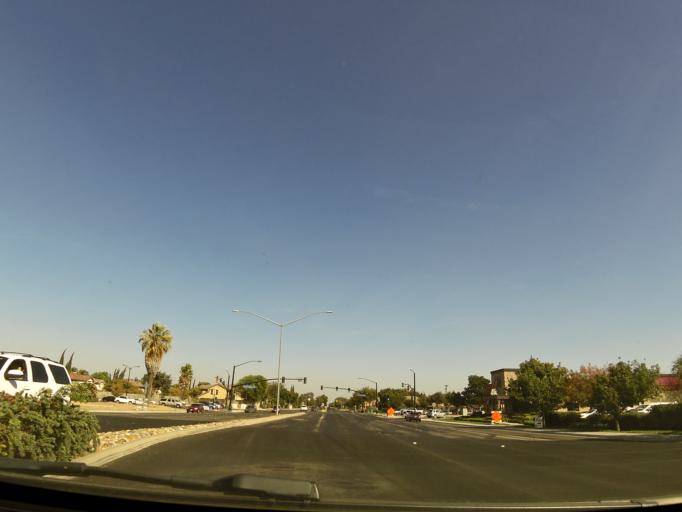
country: US
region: California
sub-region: San Joaquin County
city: Tracy
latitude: 37.7541
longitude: -121.4547
